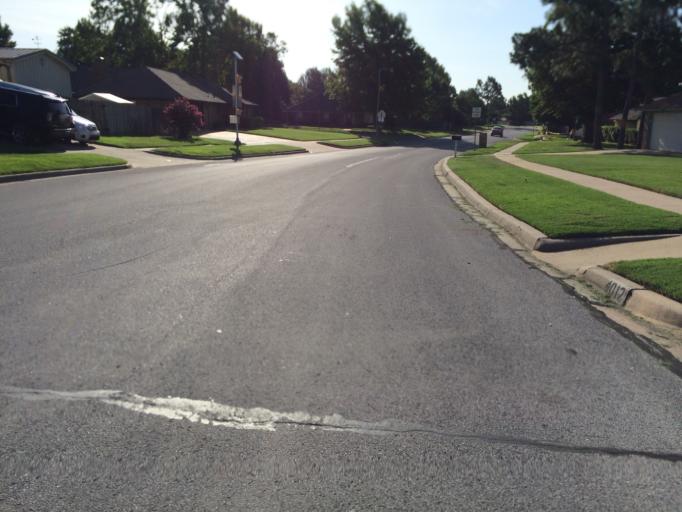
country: US
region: Oklahoma
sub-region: Cleveland County
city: Norman
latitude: 35.2240
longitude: -97.5021
